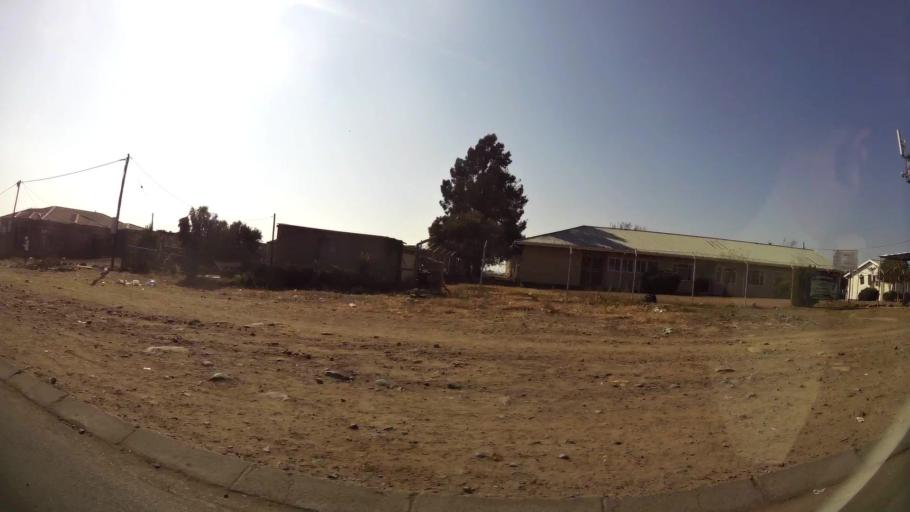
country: ZA
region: Orange Free State
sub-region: Mangaung Metropolitan Municipality
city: Bloemfontein
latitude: -29.1759
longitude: 26.2412
